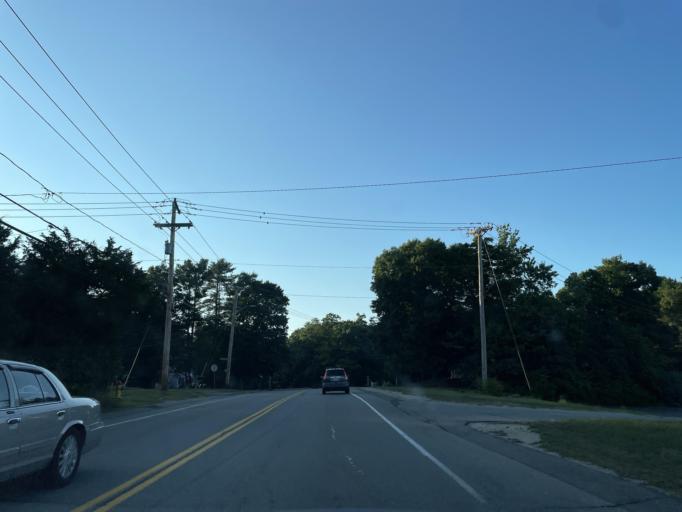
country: US
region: Massachusetts
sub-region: Plymouth County
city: Halifax
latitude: 42.0332
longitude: -70.8444
